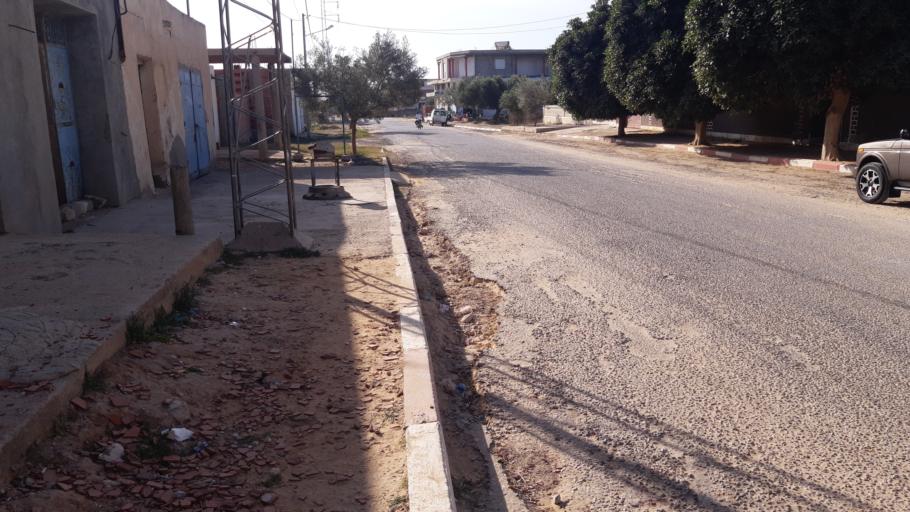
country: TN
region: Al Munastir
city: Sidi Bin Nur
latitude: 35.4799
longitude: 10.8733
